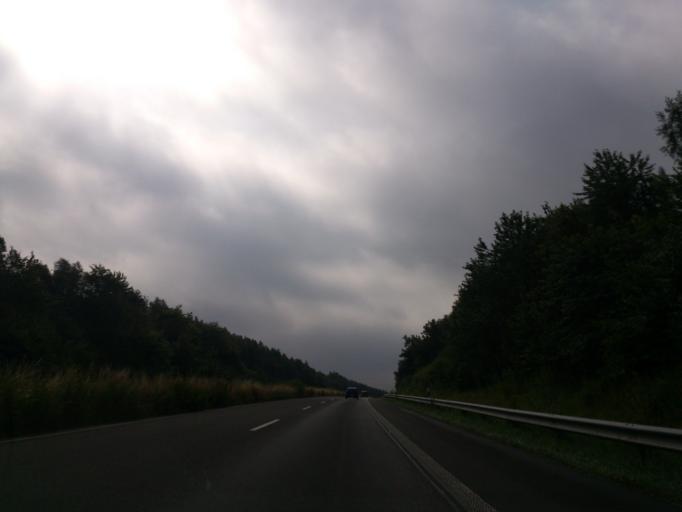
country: DE
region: Schleswig-Holstein
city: Arkebek
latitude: 54.1557
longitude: 9.2299
